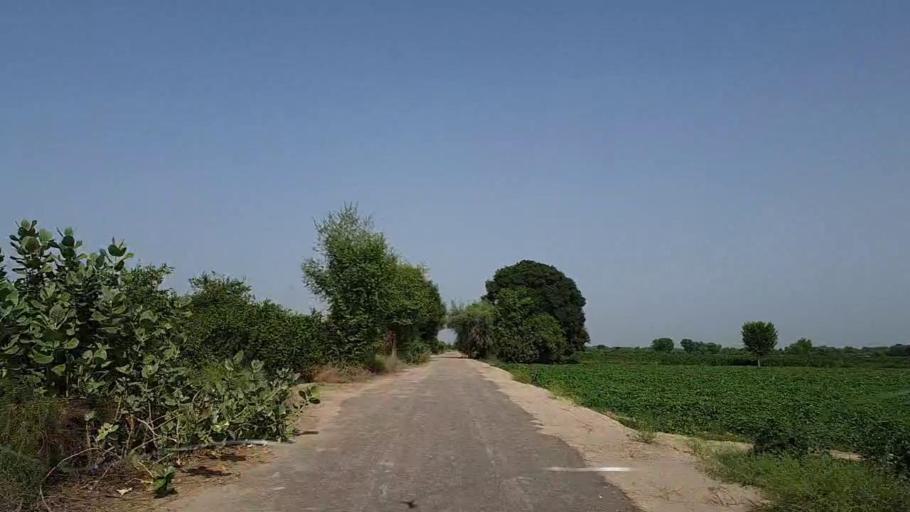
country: PK
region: Sindh
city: Kandiaro
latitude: 27.0727
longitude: 68.1442
